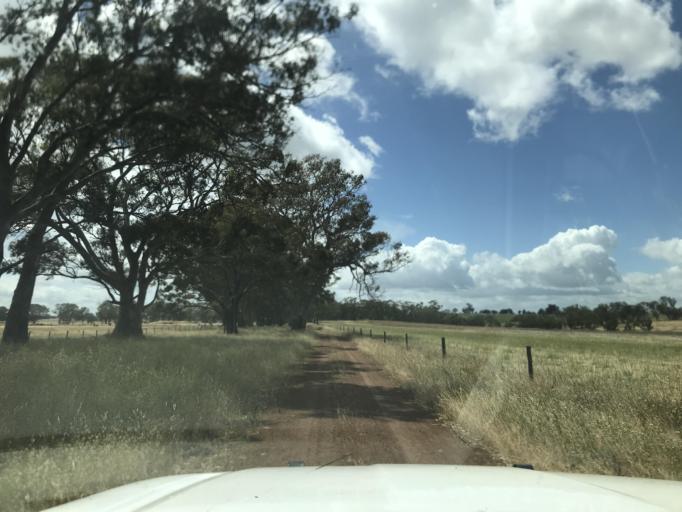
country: AU
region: South Australia
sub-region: Wattle Range
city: Penola
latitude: -37.1849
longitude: 141.4782
